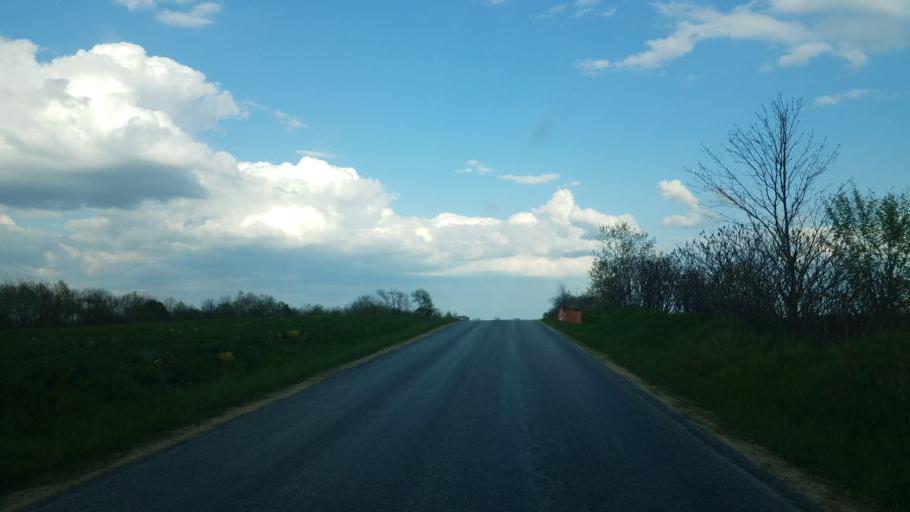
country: US
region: Wisconsin
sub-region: Vernon County
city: Hillsboro
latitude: 43.6844
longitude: -90.3793
